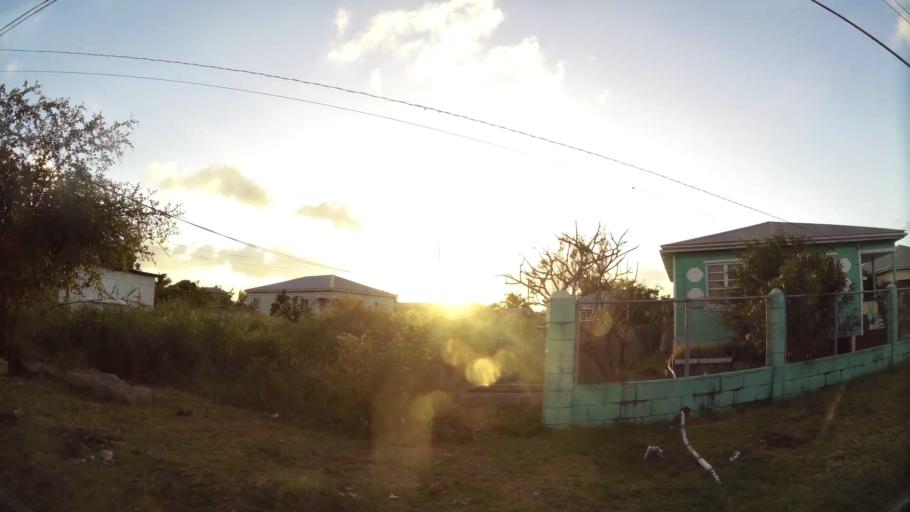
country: AG
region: Saint John
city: Saint John's
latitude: 17.1326
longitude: -61.8390
